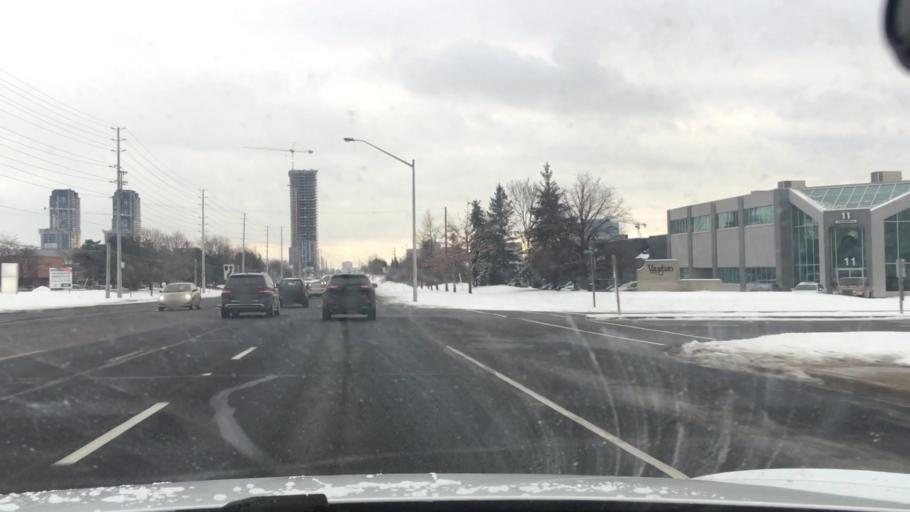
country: CA
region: Ontario
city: Vaughan
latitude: 43.8065
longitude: -79.5272
